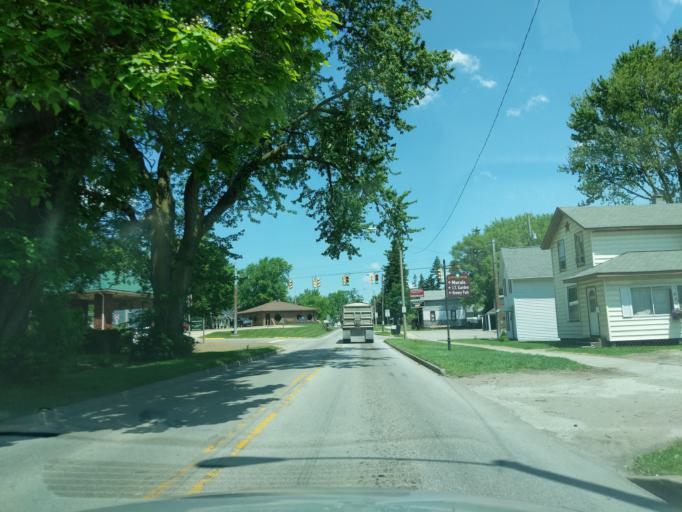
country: US
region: Indiana
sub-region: Noble County
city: Ligonier
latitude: 41.4589
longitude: -85.5869
